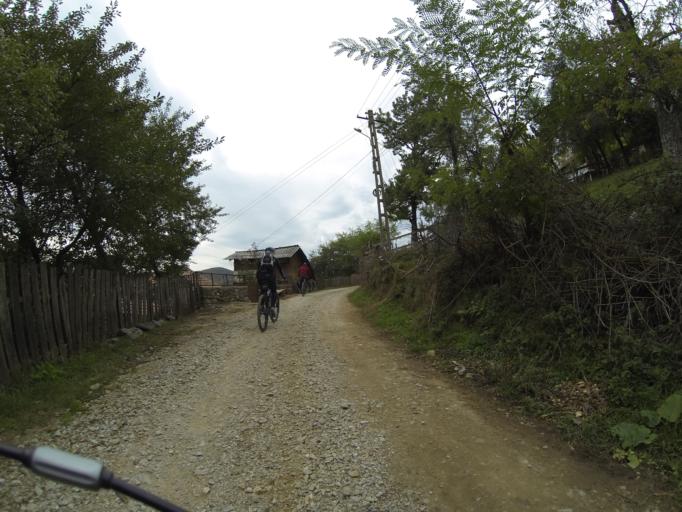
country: RO
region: Gorj
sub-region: Comuna Tismana
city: Sohodol
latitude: 45.0597
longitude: 22.8758
